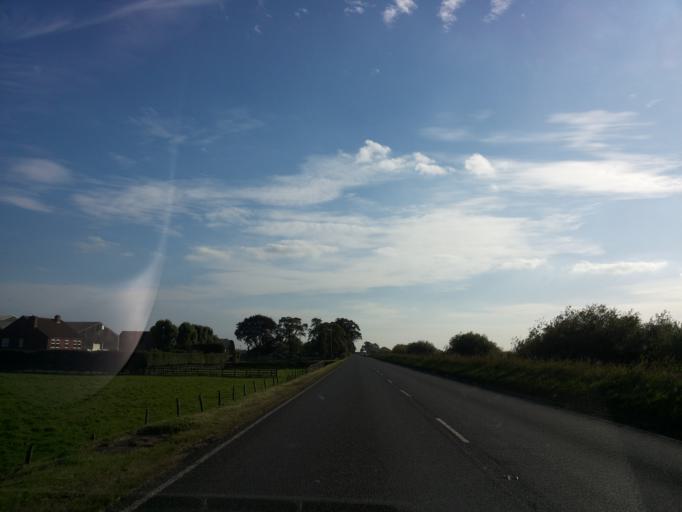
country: GB
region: England
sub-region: East Riding of Yorkshire
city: Rawcliffe
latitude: 53.6665
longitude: -0.9904
